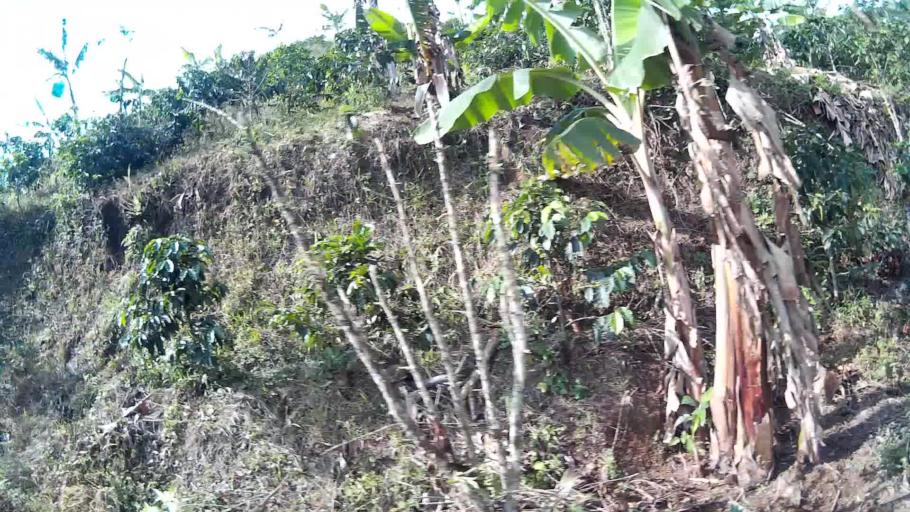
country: CO
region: Valle del Cauca
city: Ulloa
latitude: 4.7141
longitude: -75.7057
